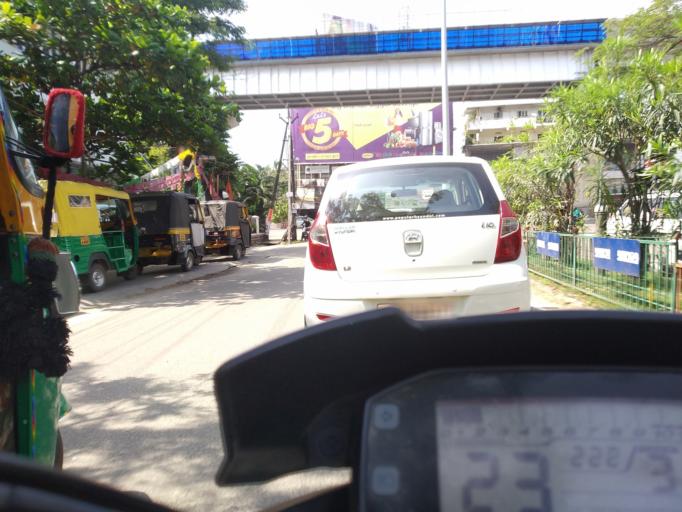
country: IN
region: Kerala
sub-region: Ernakulam
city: Cochin
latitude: 9.9652
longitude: 76.2949
